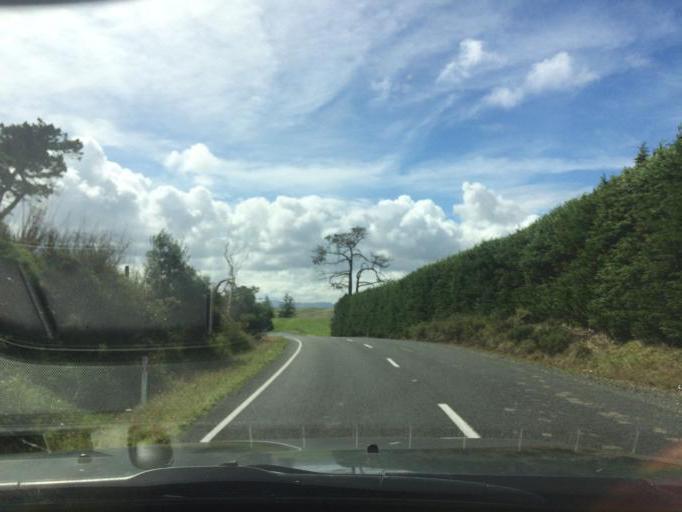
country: NZ
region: Northland
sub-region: Kaipara District
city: Dargaville
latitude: -35.9471
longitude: 173.7705
